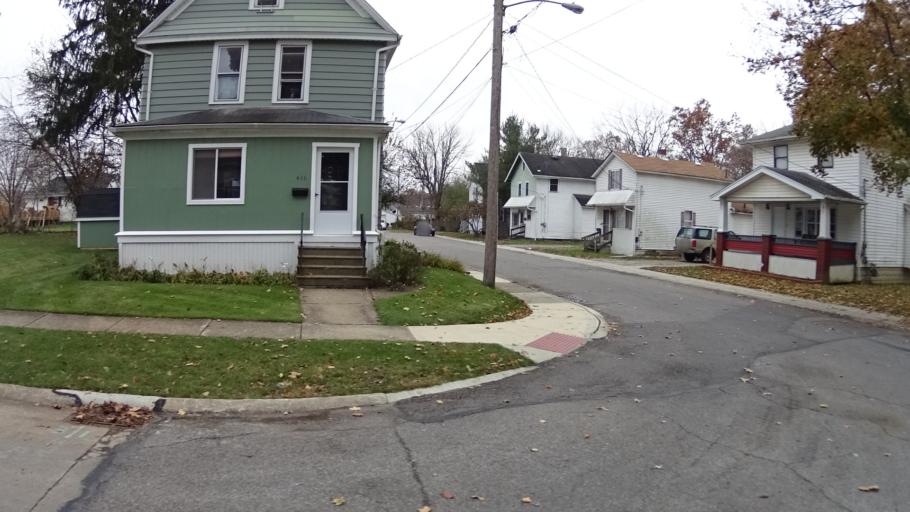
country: US
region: Ohio
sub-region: Lorain County
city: Elyria
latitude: 41.3541
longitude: -82.1124
